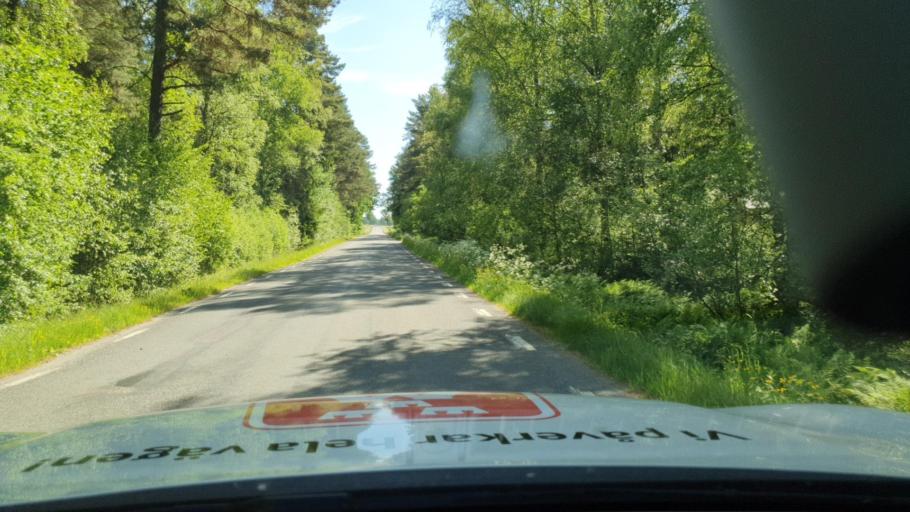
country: SE
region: Vaestra Goetaland
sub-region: Skovde Kommun
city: Skultorp
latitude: 58.2593
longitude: 13.8871
